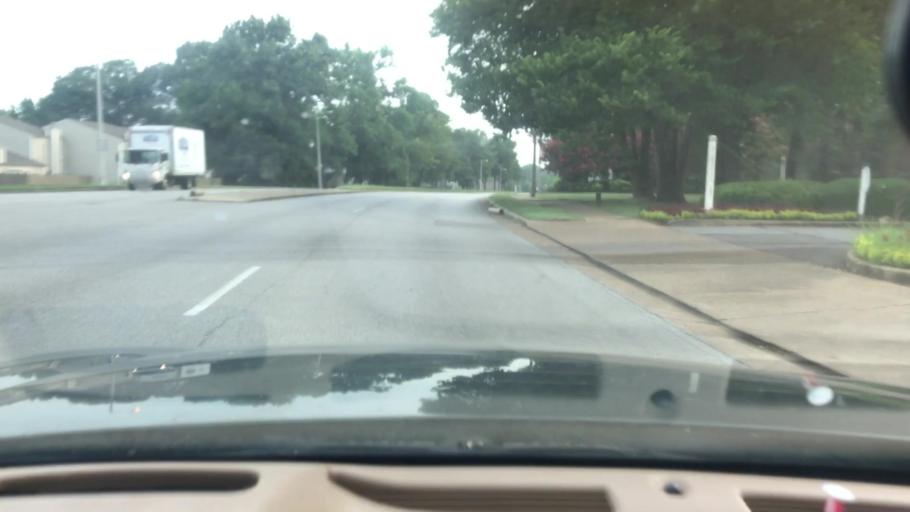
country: US
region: Tennessee
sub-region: Shelby County
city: Bartlett
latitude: 35.1766
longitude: -89.8714
